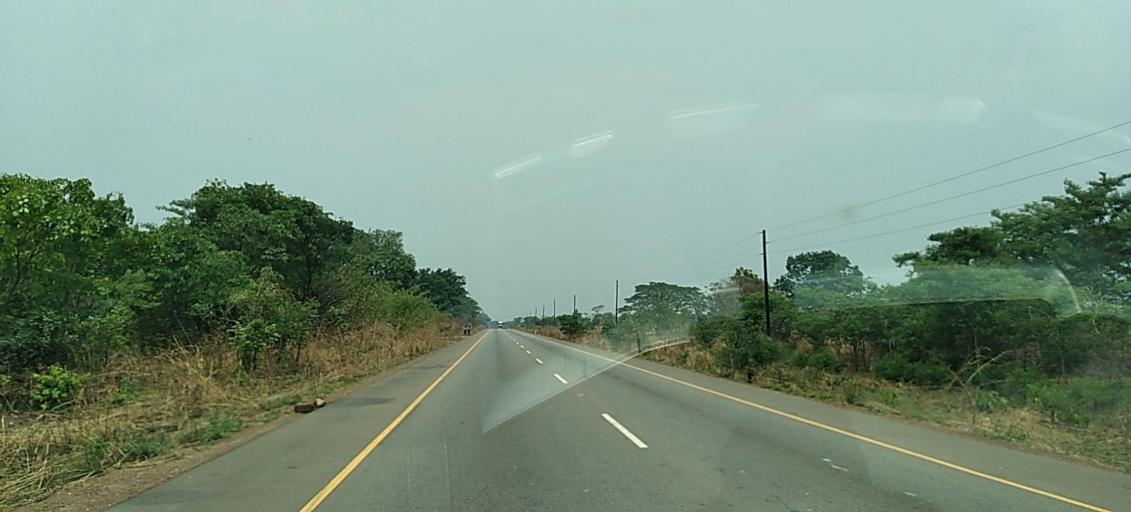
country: ZM
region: Copperbelt
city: Chililabombwe
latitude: -12.5090
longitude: 27.5507
